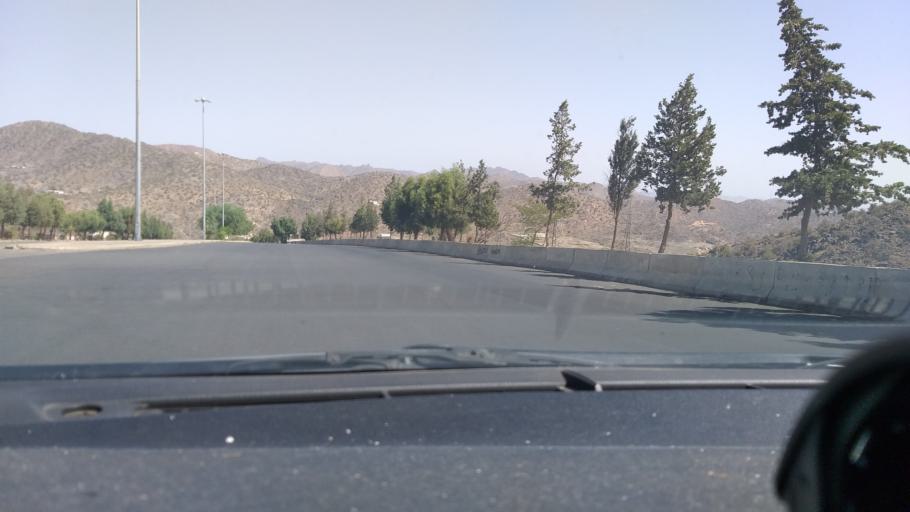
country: SA
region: Makkah
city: Ash Shafa
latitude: 21.0841
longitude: 40.3143
